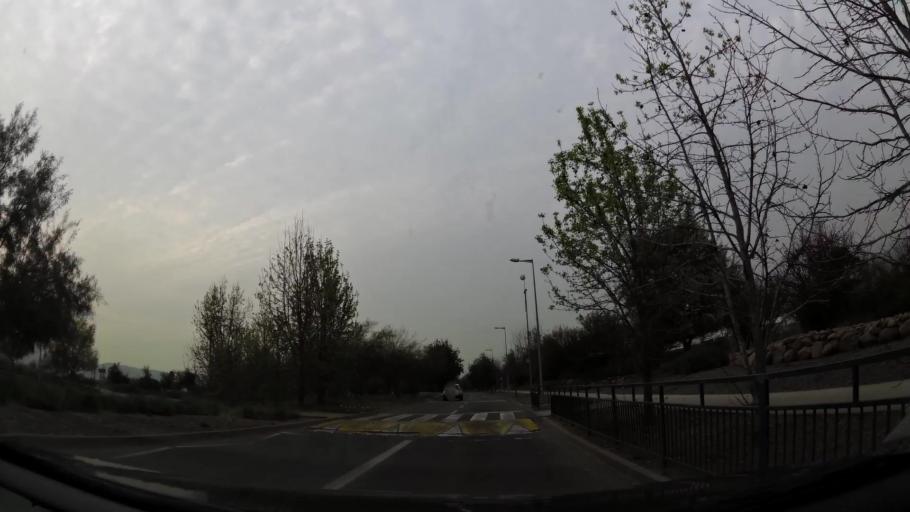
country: CL
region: Santiago Metropolitan
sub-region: Provincia de Chacabuco
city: Chicureo Abajo
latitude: -33.2771
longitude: -70.6255
